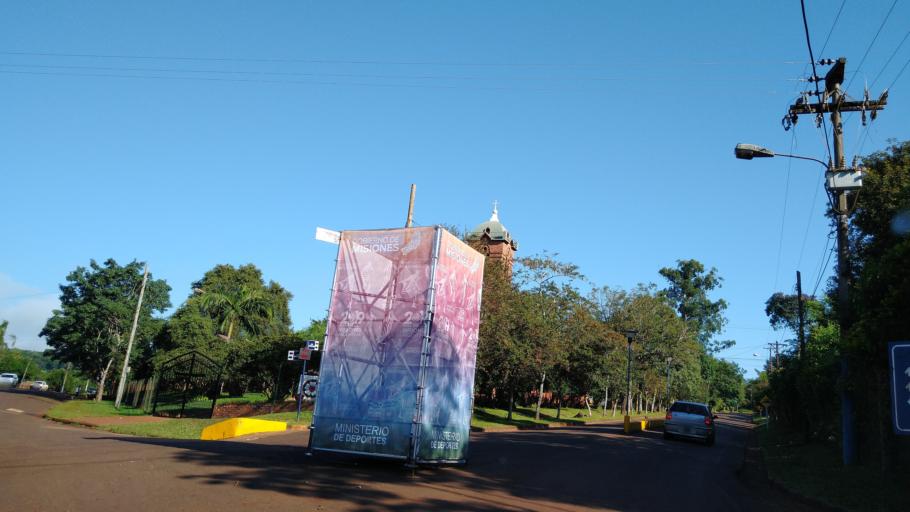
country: AR
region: Misiones
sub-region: Departamento de Montecarlo
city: Montecarlo
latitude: -26.5616
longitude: -54.7755
